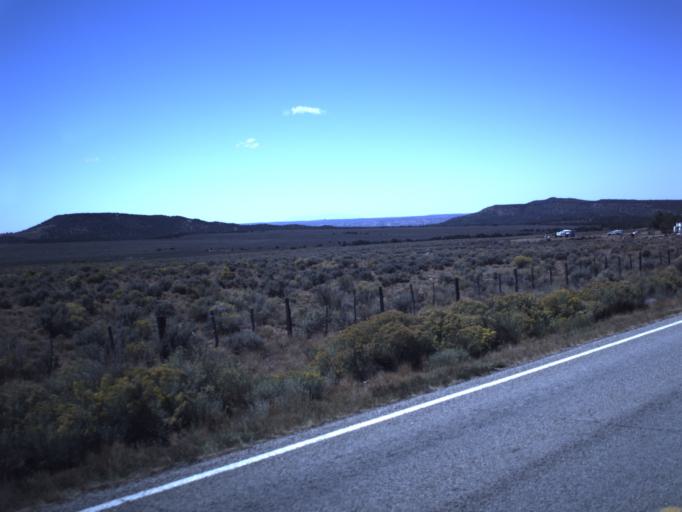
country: US
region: Utah
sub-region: Grand County
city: Moab
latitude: 38.3121
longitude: -109.3006
